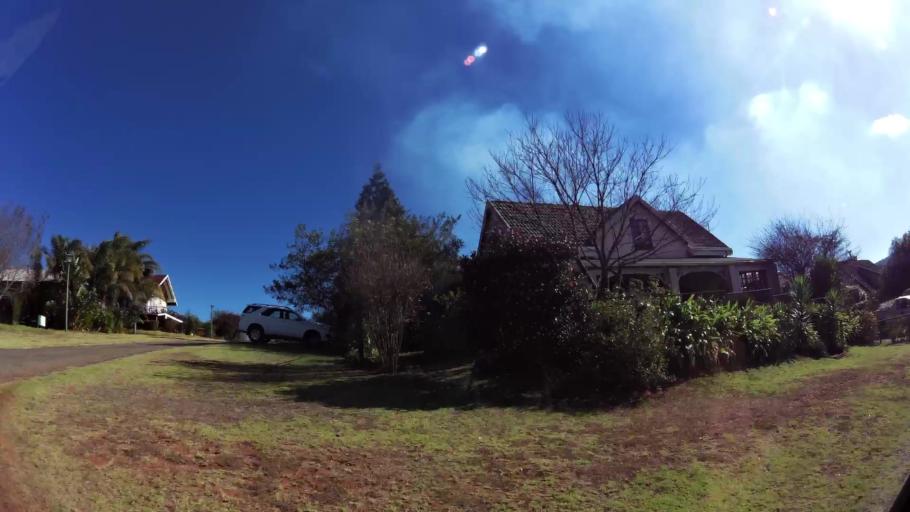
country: ZA
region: Limpopo
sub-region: Capricorn District Municipality
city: Mankoeng
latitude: -23.9446
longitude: 29.9410
